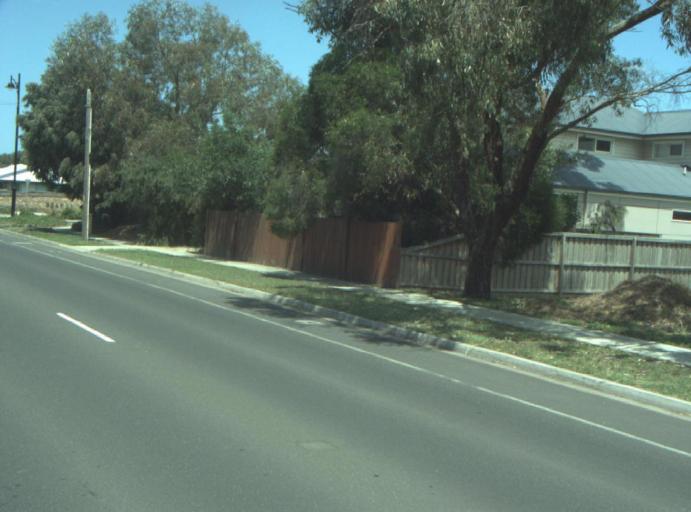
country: AU
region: Victoria
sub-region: Greater Geelong
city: Leopold
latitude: -38.2766
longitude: 144.4882
